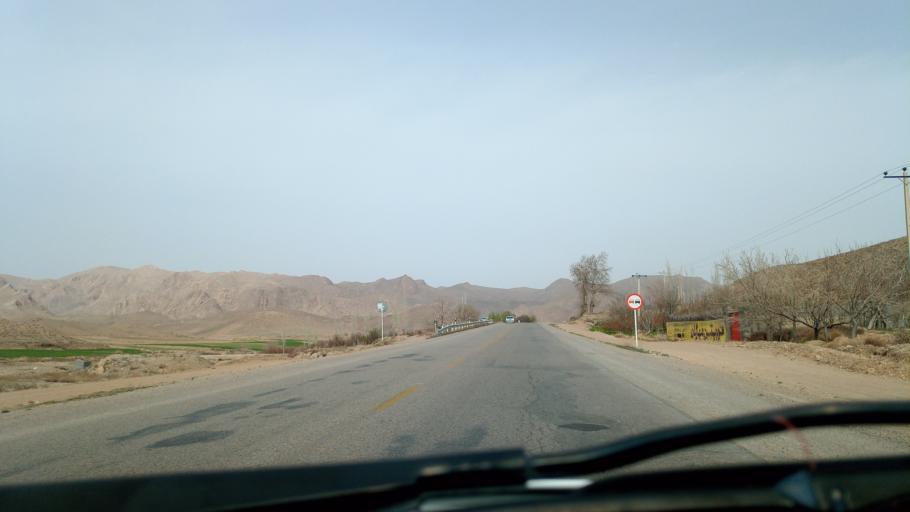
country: IR
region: Khorasan-e Shomali
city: Esfarayen
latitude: 37.1438
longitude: 57.4109
